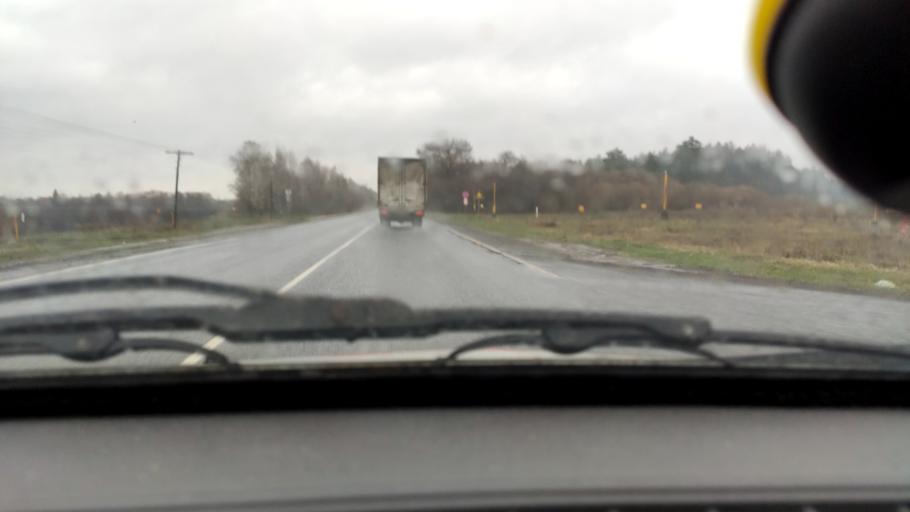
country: RU
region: Samara
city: Povolzhskiy
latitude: 53.6037
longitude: 49.6014
